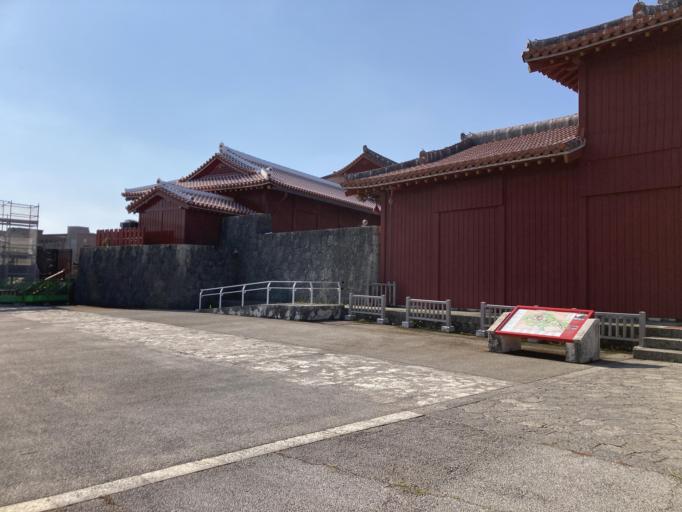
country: JP
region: Okinawa
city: Naha-shi
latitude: 26.2174
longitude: 127.7187
